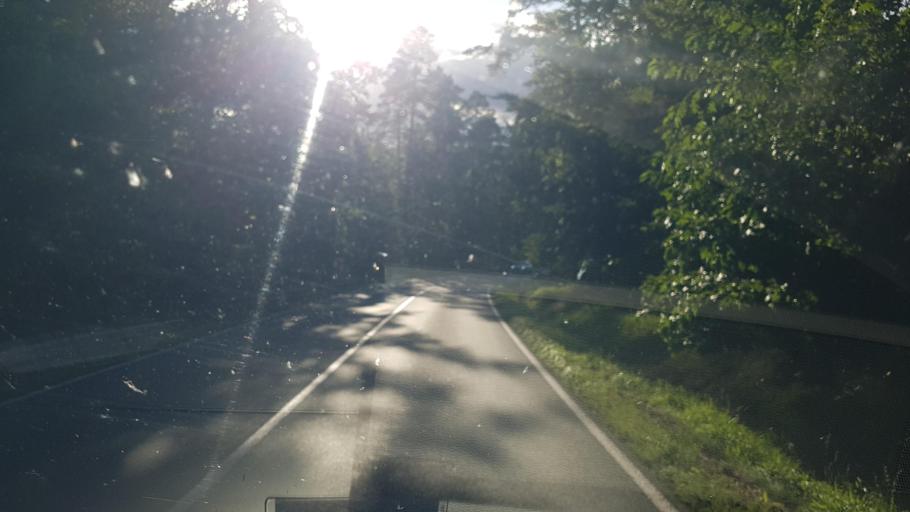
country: DE
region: Thuringia
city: Harra
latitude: 50.4500
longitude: 11.7036
